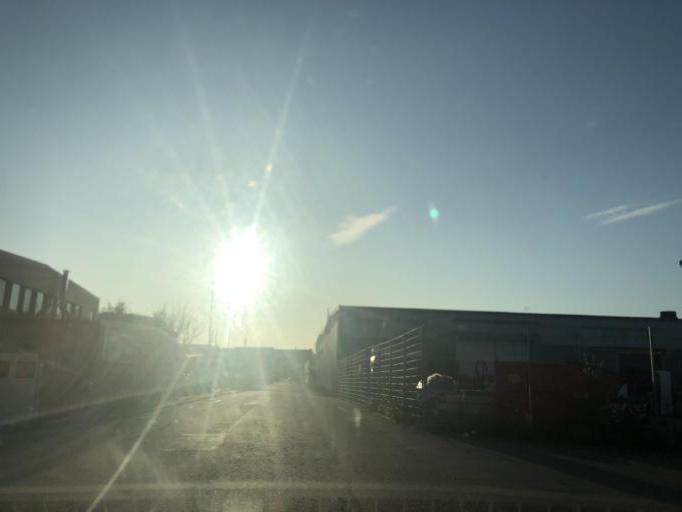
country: SE
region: Vaestra Goetaland
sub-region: Goteborg
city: Eriksbo
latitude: 57.7488
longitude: 11.9985
